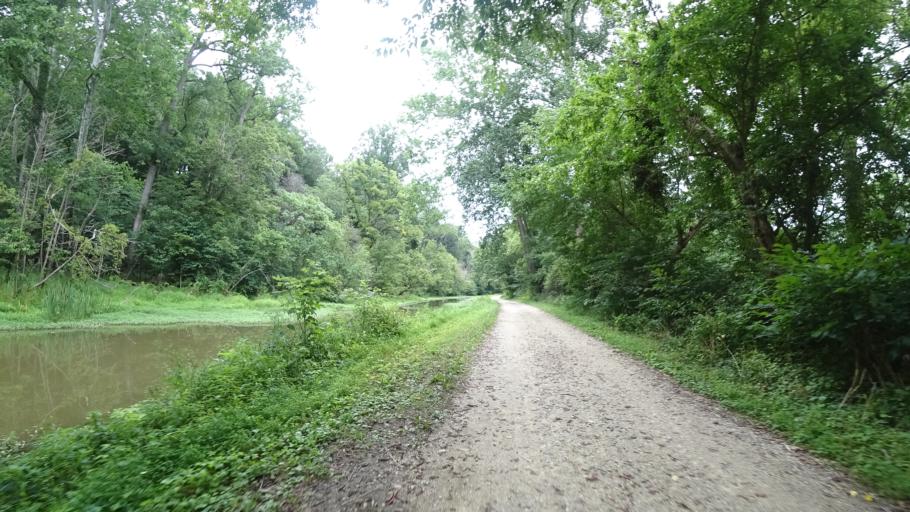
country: US
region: Maryland
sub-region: Montgomery County
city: Travilah
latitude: 39.0328
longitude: -77.2468
